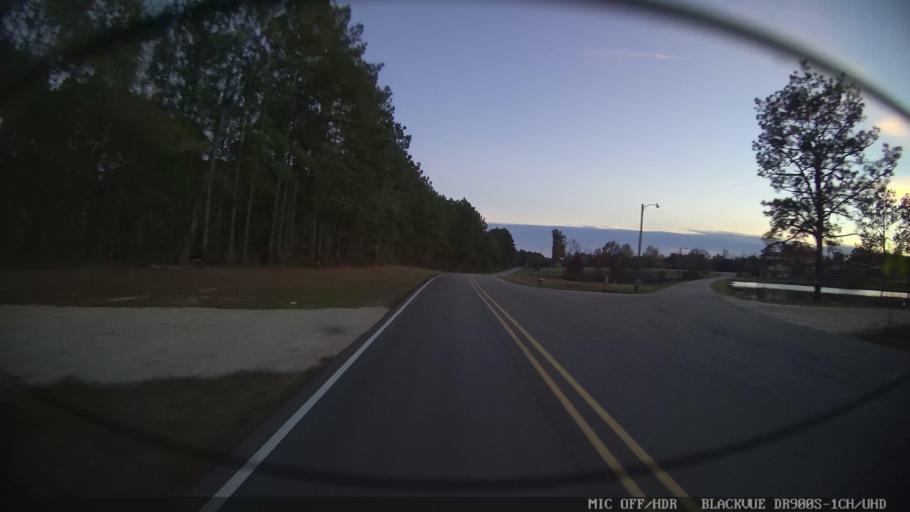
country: US
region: Mississippi
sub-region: Perry County
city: New Augusta
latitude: 31.0712
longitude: -89.1852
